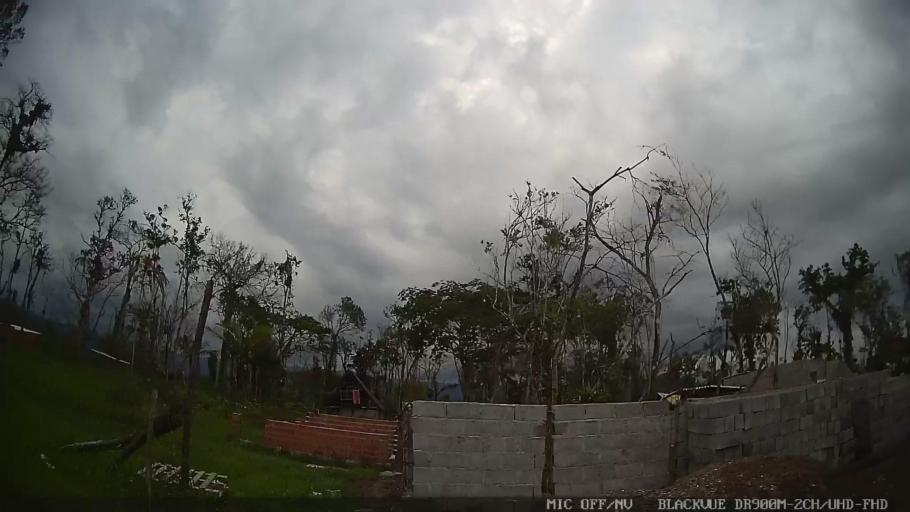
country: BR
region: Sao Paulo
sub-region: Caraguatatuba
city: Caraguatatuba
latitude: -23.6754
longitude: -45.4569
